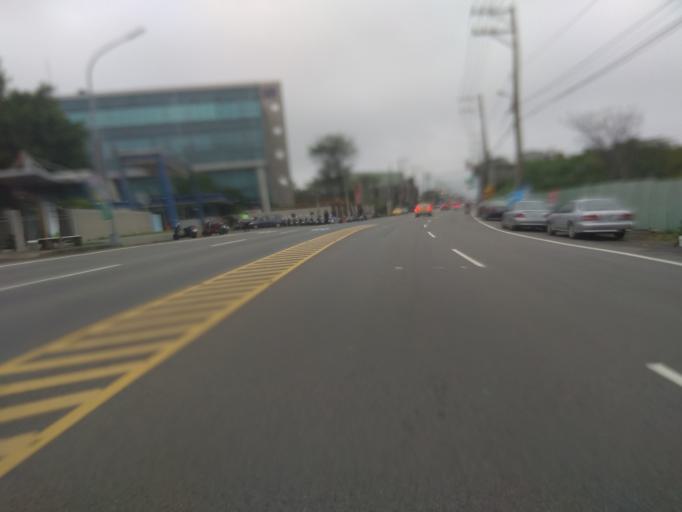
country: TW
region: Taiwan
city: Taoyuan City
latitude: 25.0213
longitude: 121.1193
